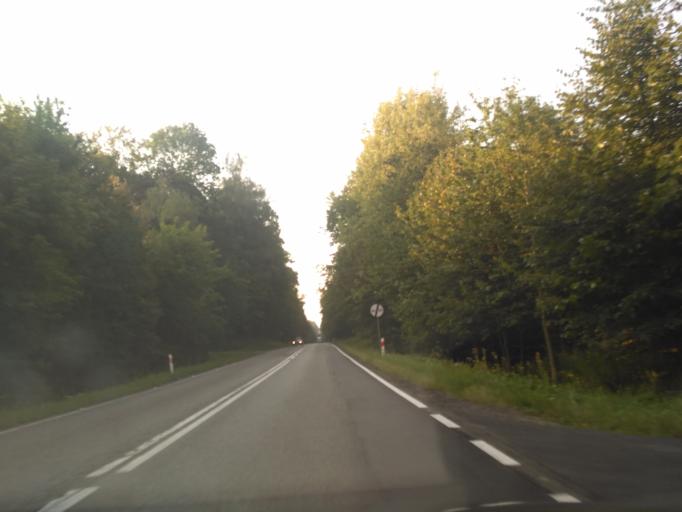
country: PL
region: Lublin Voivodeship
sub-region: Powiat krasnicki
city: Szastarka
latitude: 50.8598
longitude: 22.2807
